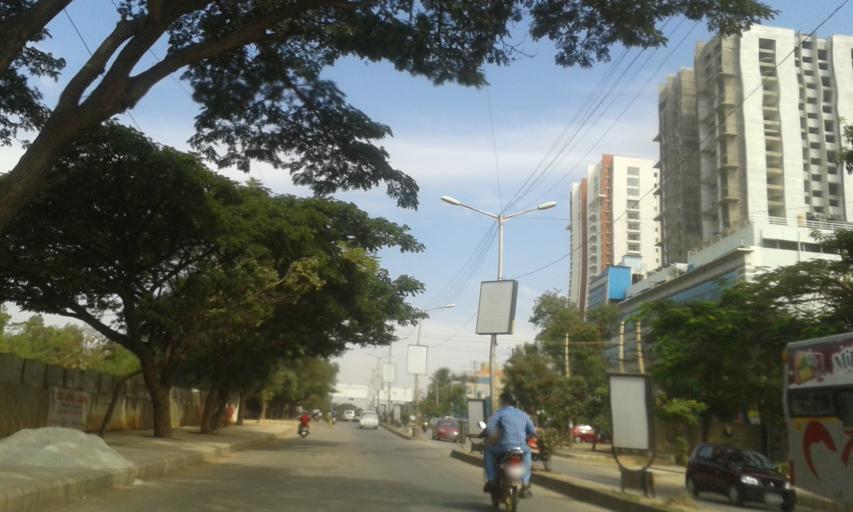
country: IN
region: Karnataka
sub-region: Bangalore Rural
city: Hoskote
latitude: 12.9744
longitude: 77.7505
